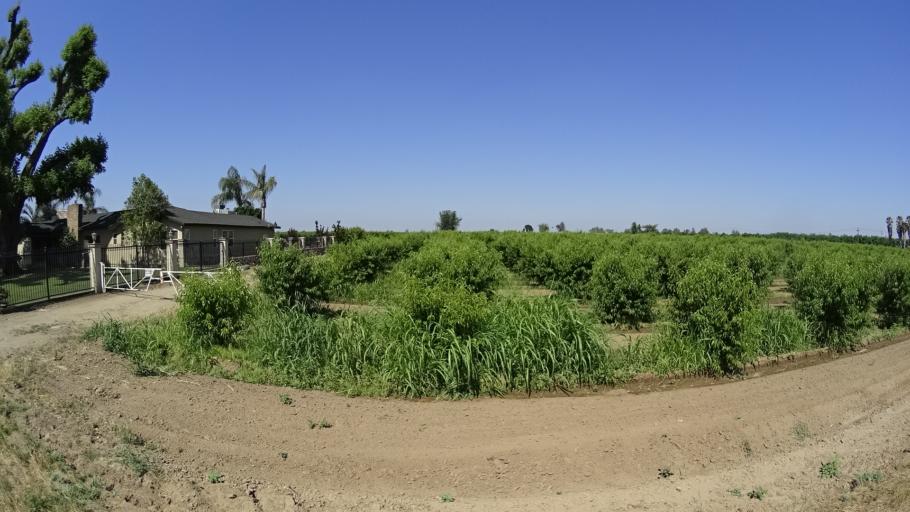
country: US
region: California
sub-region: Fresno County
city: Kingsburg
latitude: 36.4797
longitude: -119.5507
